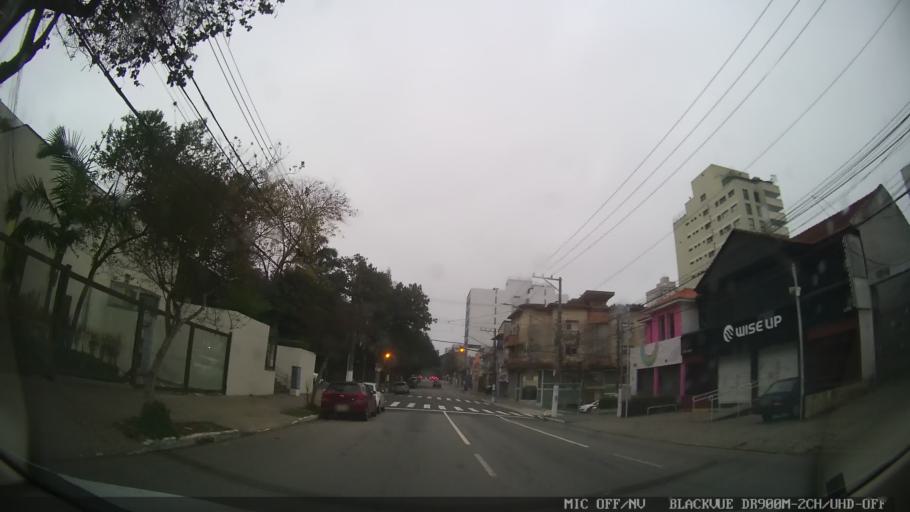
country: BR
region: Sao Paulo
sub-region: Sao Paulo
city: Sao Paulo
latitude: -23.5872
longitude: -46.6074
